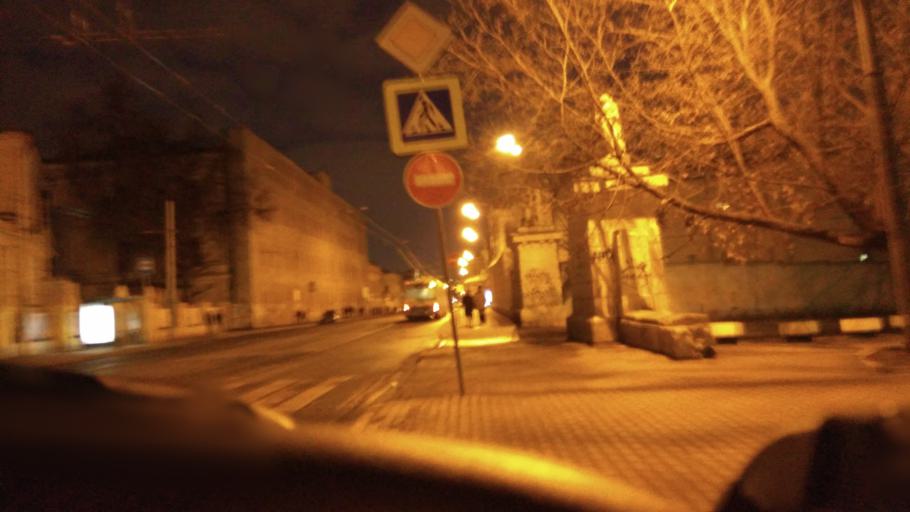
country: RU
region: Moscow
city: Zamoskvorech'ye
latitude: 55.7530
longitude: 37.6390
